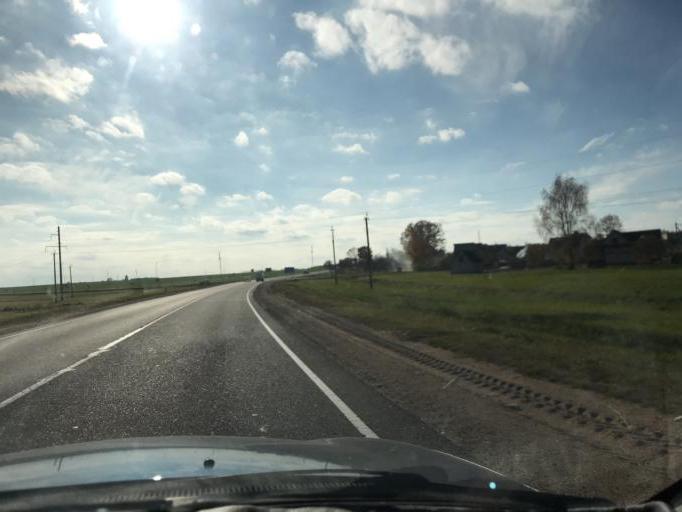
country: BY
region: Grodnenskaya
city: Voranava
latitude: 54.1479
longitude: 25.3268
